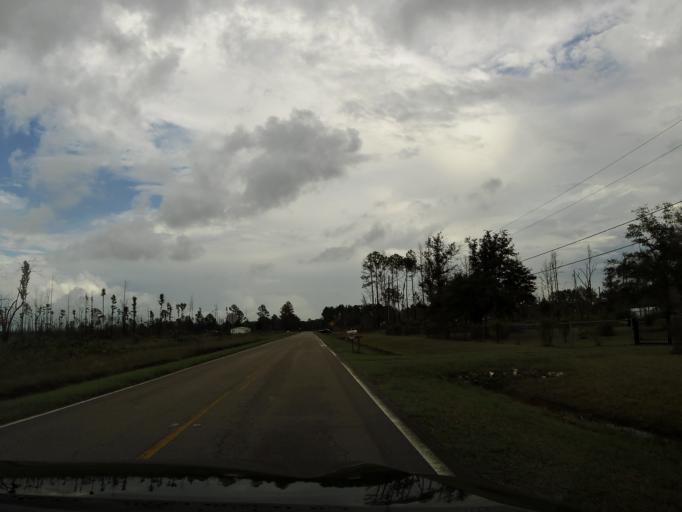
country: US
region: Florida
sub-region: Duval County
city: Baldwin
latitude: 30.4109
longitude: -82.0279
